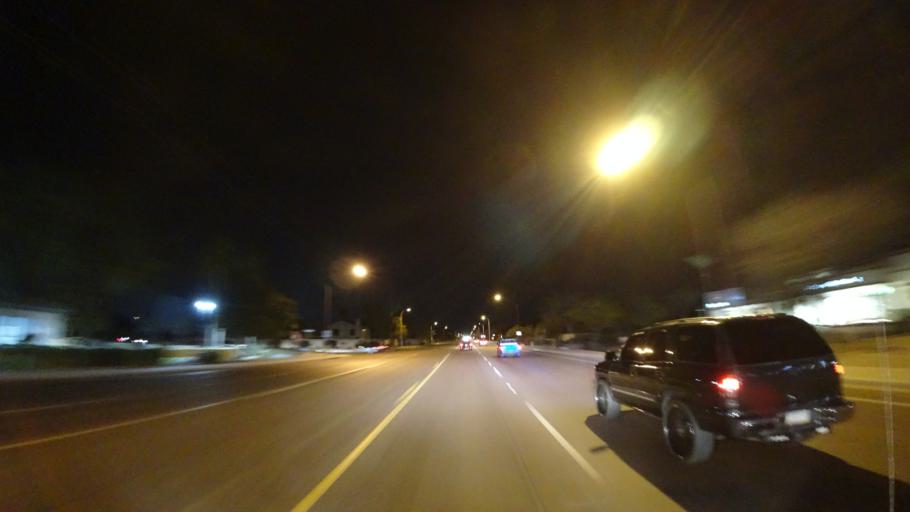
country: US
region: Arizona
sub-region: Maricopa County
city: Gilbert
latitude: 33.3369
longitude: -111.8069
